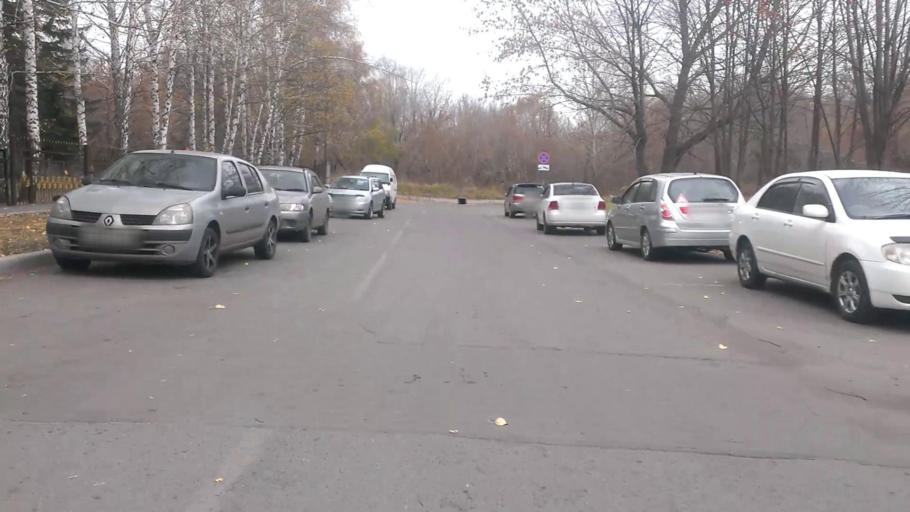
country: RU
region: Altai Krai
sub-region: Gorod Barnaulskiy
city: Barnaul
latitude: 53.3668
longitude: 83.7188
